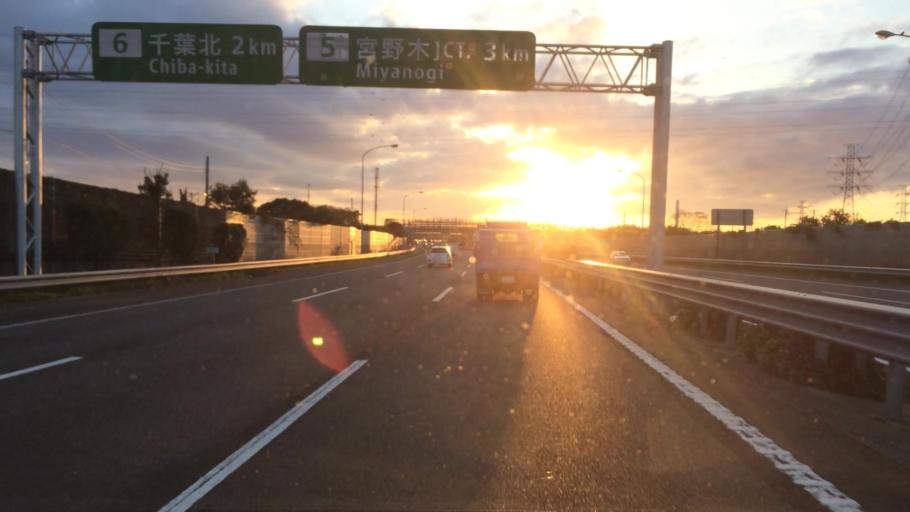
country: JP
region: Chiba
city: Yotsukaido
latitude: 35.6788
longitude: 140.1381
